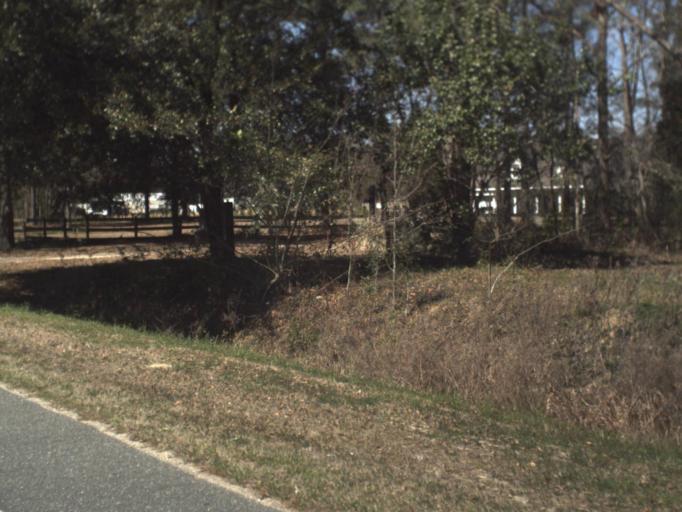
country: US
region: Florida
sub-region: Washington County
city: Chipley
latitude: 30.7880
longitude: -85.4293
